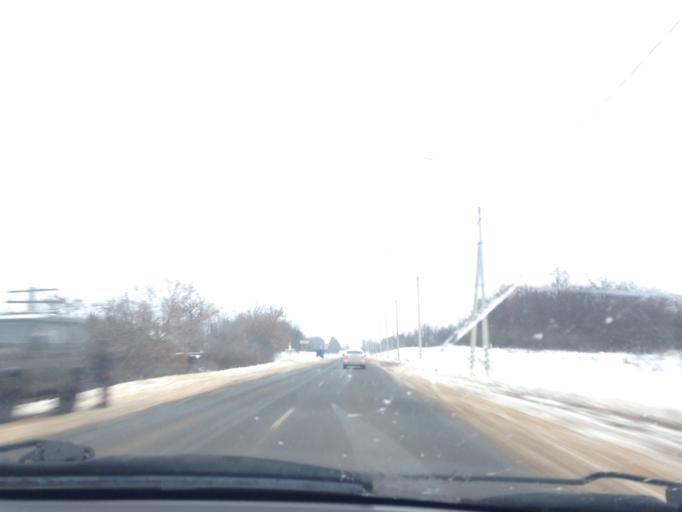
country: RU
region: Tula
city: Shchekino
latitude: 53.9743
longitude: 37.4994
